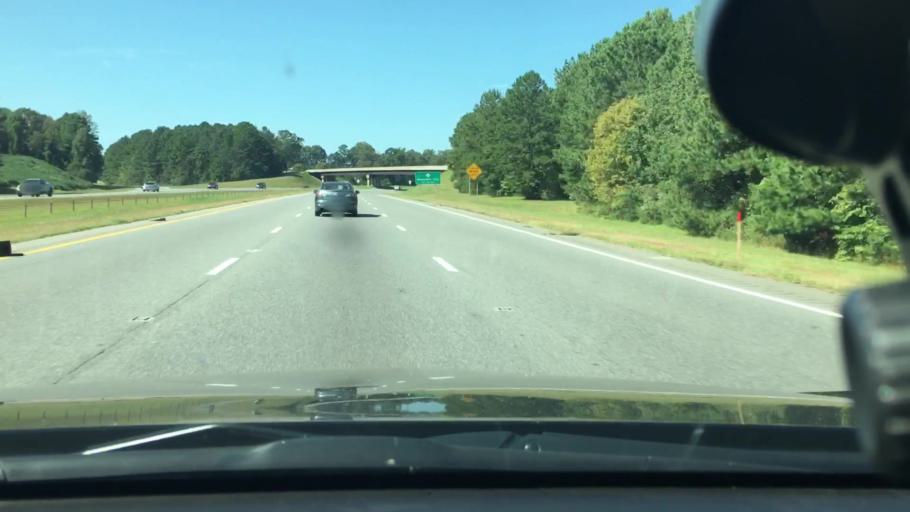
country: US
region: North Carolina
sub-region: Cleveland County
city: Kings Mountain
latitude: 35.2433
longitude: -81.3185
